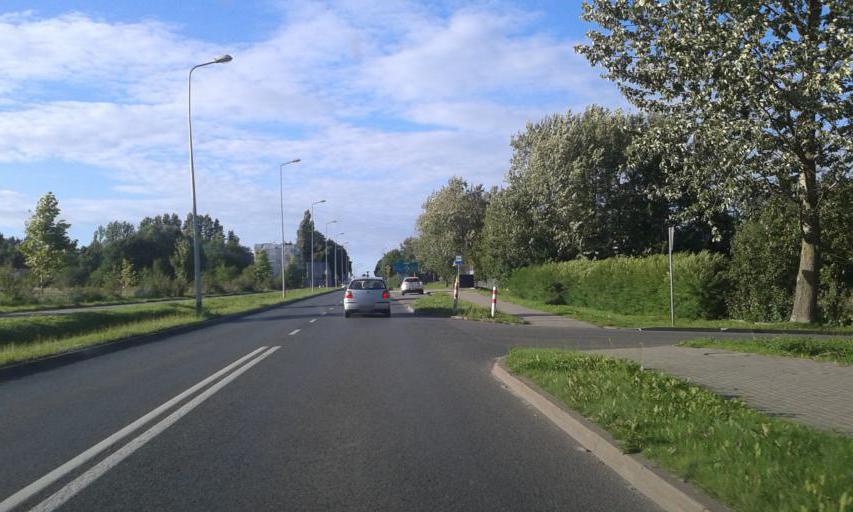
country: PL
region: West Pomeranian Voivodeship
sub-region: Koszalin
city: Koszalin
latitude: 54.1730
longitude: 16.1845
